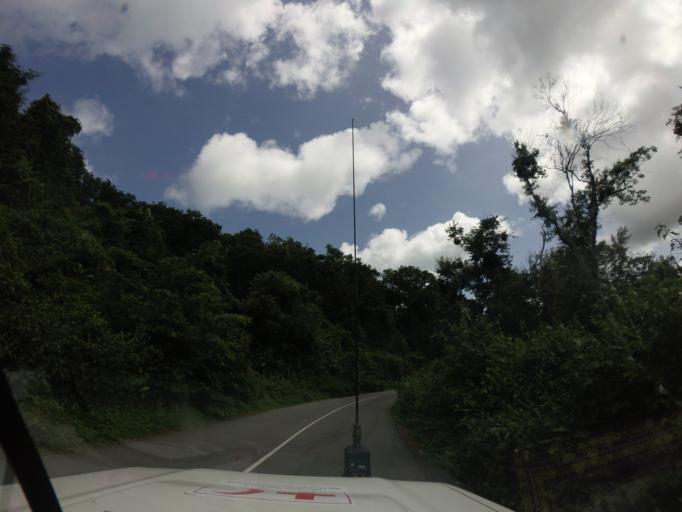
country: GN
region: Mamou
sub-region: Mamou Prefecture
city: Mamou
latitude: 10.2910
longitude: -11.9608
